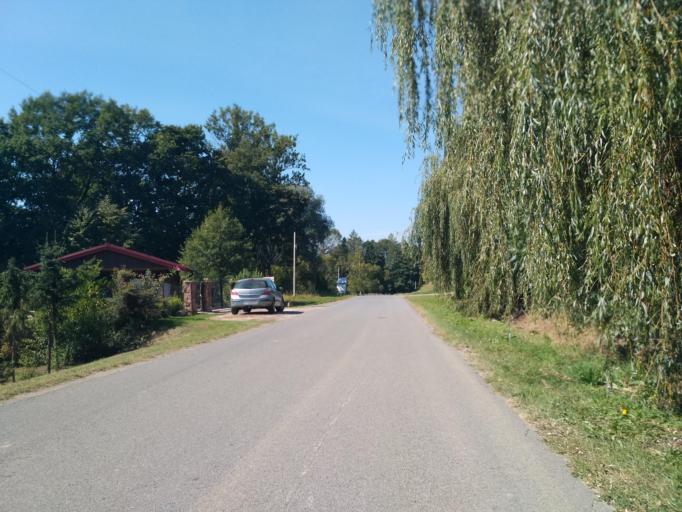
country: PL
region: Subcarpathian Voivodeship
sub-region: Powiat brzozowski
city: Niebocko
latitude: 49.6405
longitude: 22.1163
